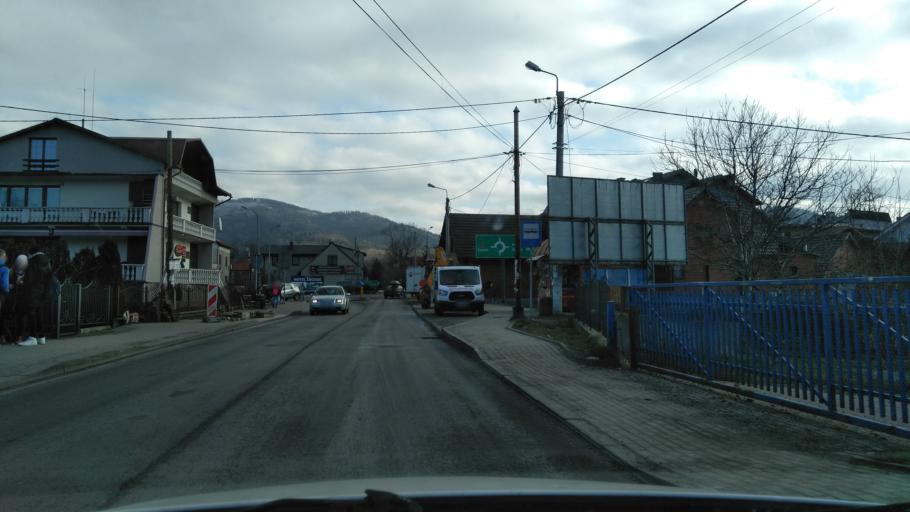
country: PL
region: Silesian Voivodeship
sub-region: Powiat zywiecki
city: Milowka
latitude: 49.5594
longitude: 19.0856
